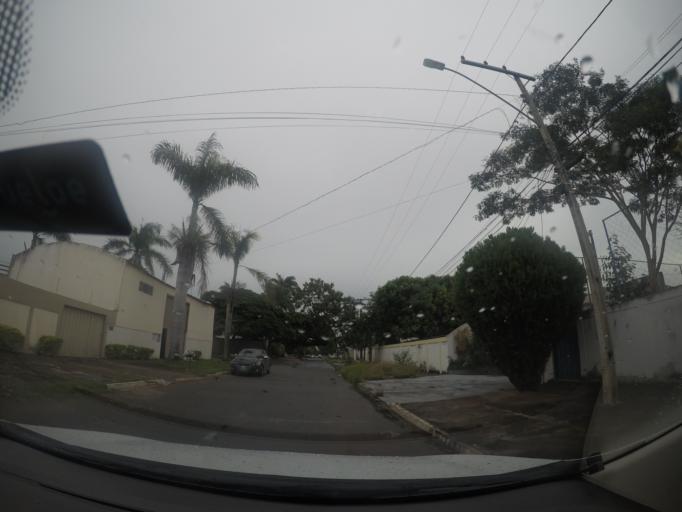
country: BR
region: Goias
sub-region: Goiania
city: Goiania
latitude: -16.6323
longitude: -49.2310
